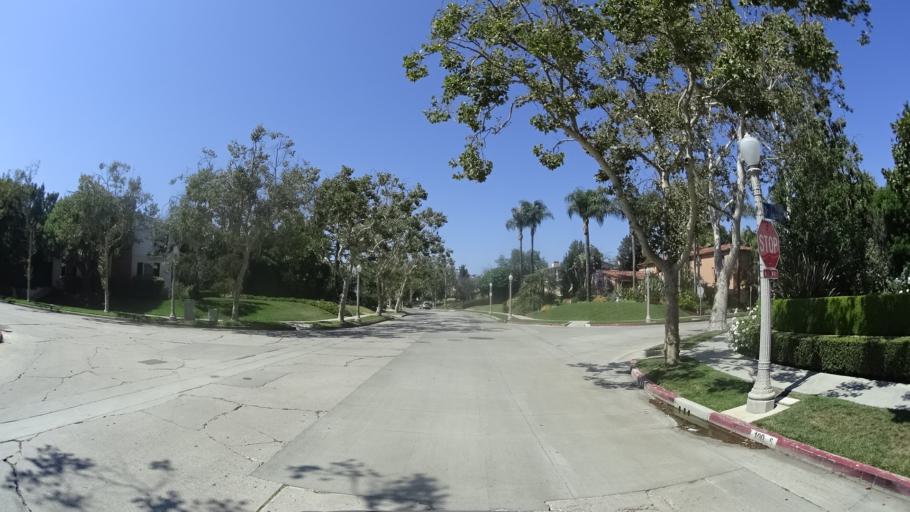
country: US
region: California
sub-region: Los Angeles County
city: Hollywood
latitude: 34.0736
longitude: -118.3345
